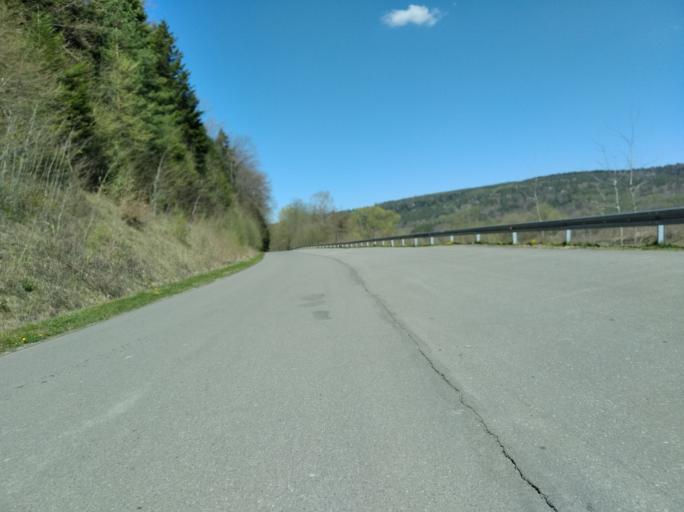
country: PL
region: Subcarpathian Voivodeship
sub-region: Powiat brzozowski
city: Dydnia
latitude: 49.6850
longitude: 22.2386
